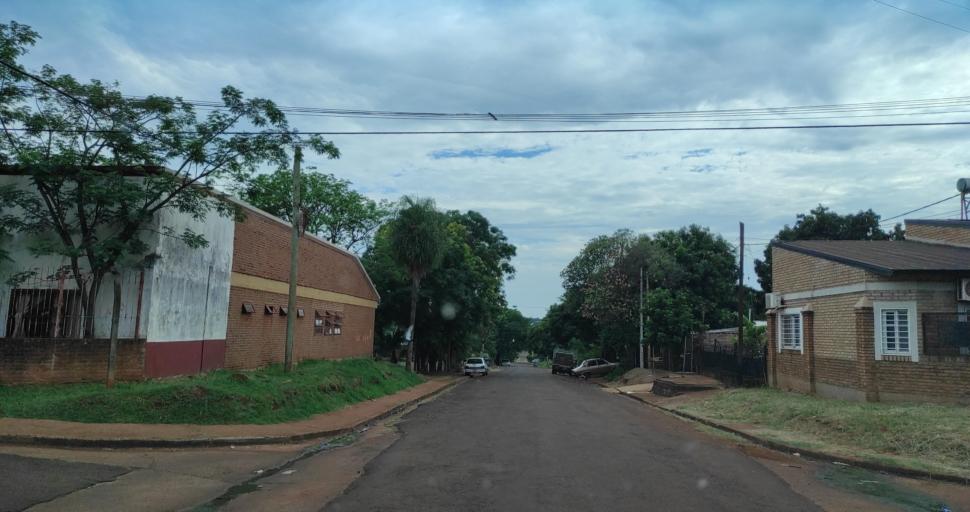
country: AR
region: Misiones
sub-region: Departamento de Capital
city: Posadas
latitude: -27.3892
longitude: -55.9300
